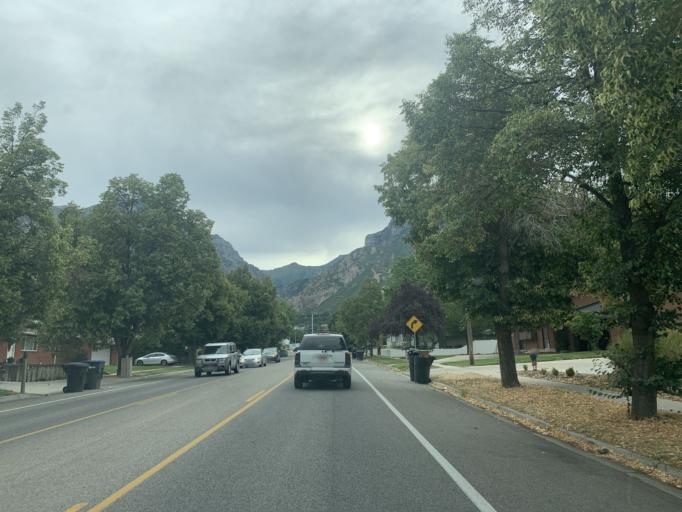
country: US
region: Utah
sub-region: Utah County
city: Provo
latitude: 40.2630
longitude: -111.6495
